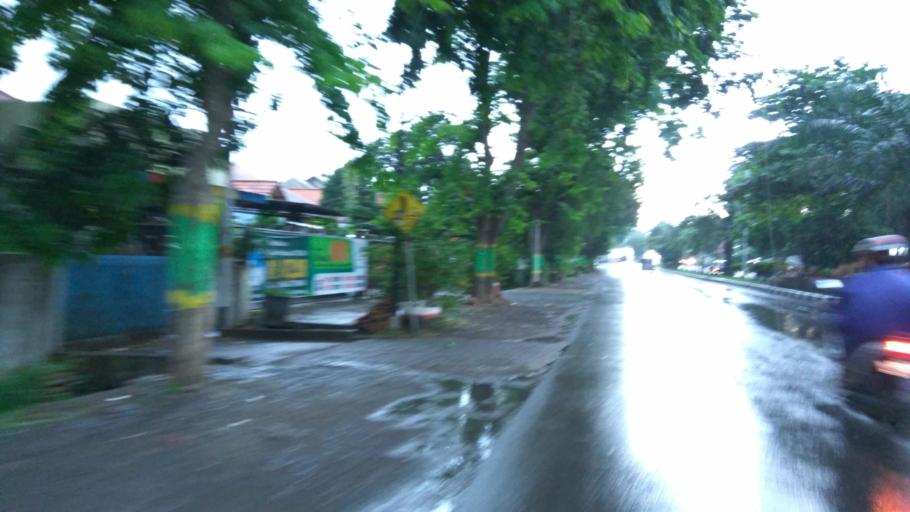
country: ID
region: Central Java
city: Semarang
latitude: -6.9875
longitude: 110.3886
